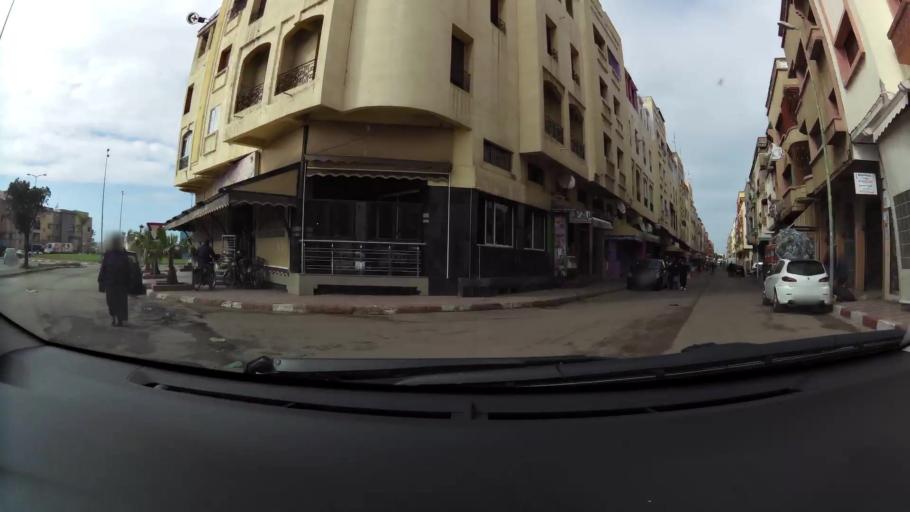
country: MA
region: Grand Casablanca
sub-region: Mohammedia
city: Mohammedia
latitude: 33.6848
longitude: -7.3789
